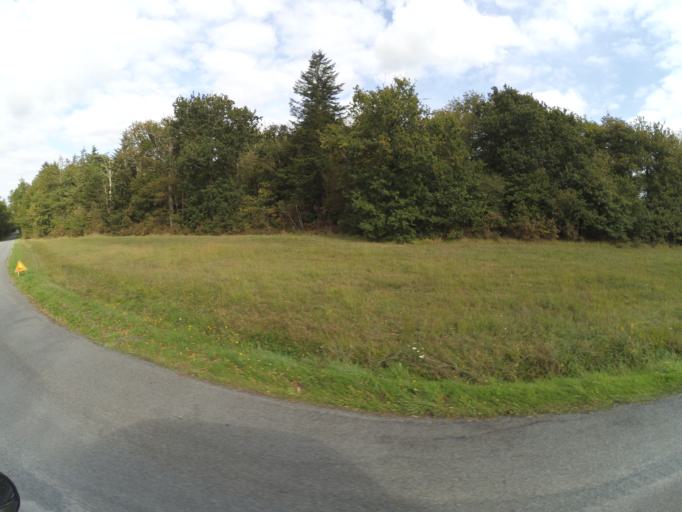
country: FR
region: Pays de la Loire
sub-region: Departement de la Loire-Atlantique
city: Bouvron
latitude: 47.4504
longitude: -1.8196
